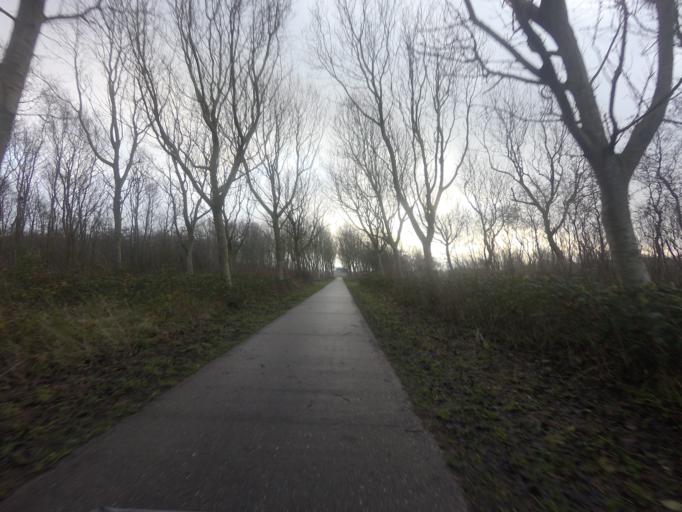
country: NL
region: North Holland
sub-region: Gemeente Texel
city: Den Burg
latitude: 53.1603
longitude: 4.8525
